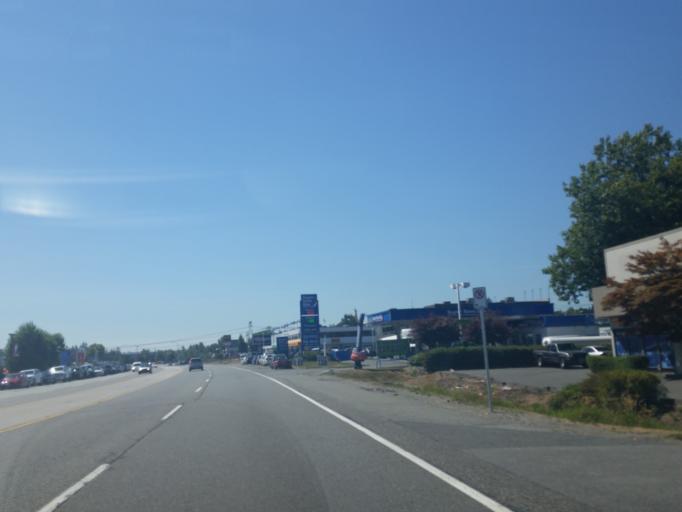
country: CA
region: British Columbia
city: Langley
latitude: 49.1077
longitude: -122.6847
